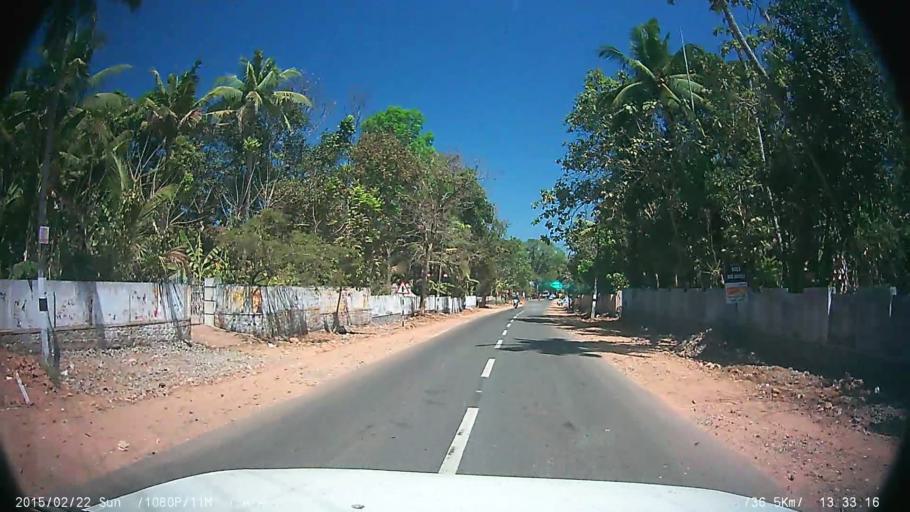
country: IN
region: Kerala
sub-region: Kottayam
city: Changanacheri
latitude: 9.4805
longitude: 76.5906
